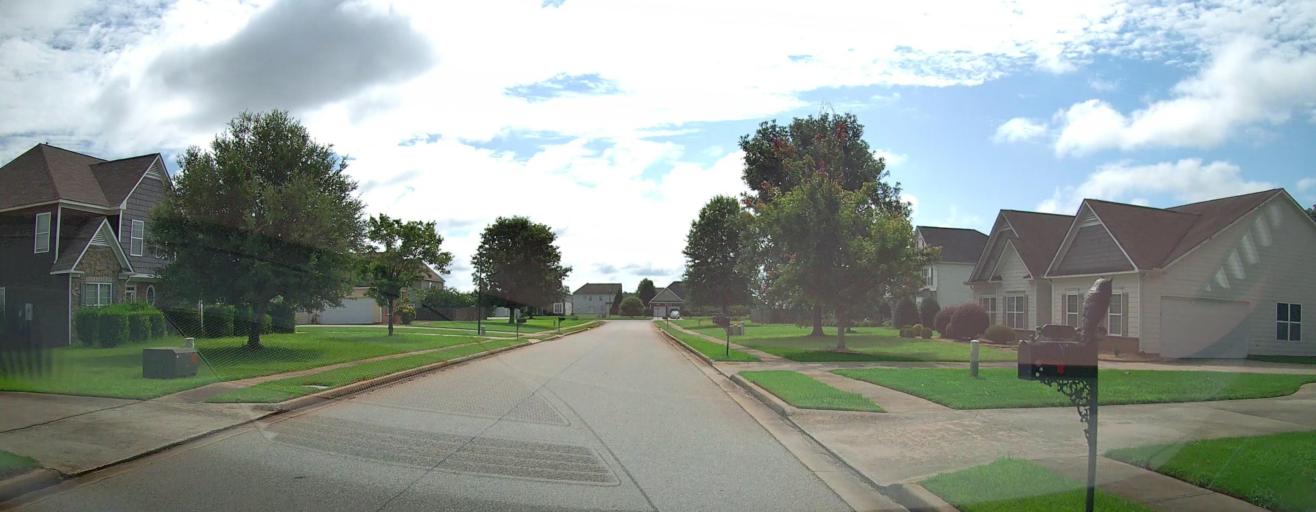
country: US
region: Georgia
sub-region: Peach County
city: Byron
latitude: 32.6306
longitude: -83.7390
